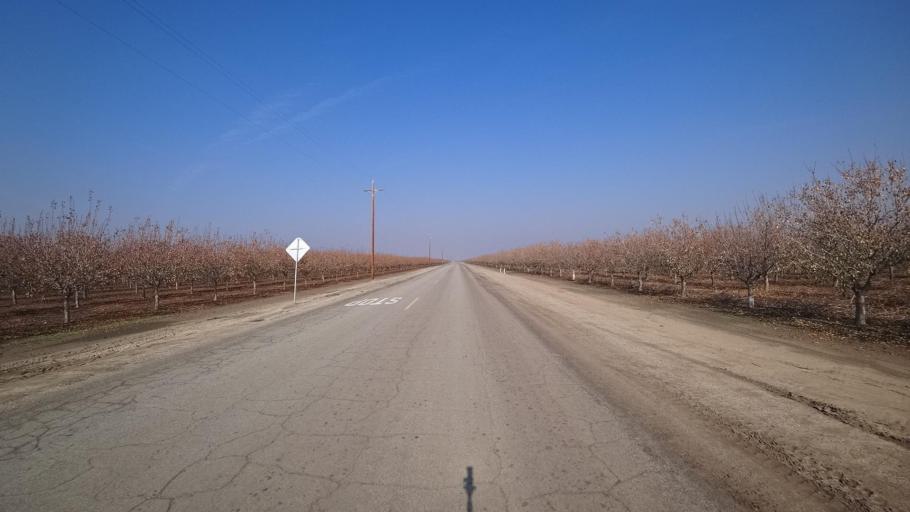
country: US
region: California
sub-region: Kern County
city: Buttonwillow
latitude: 35.3416
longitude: -119.3945
